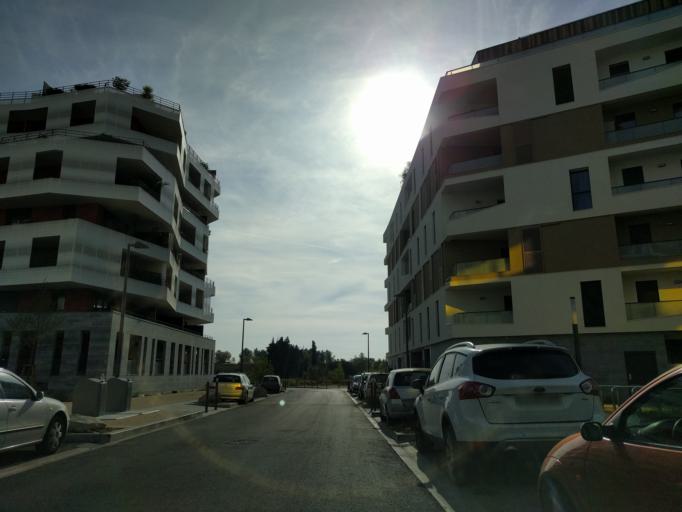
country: FR
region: Languedoc-Roussillon
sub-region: Departement de l'Herault
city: Montpellier
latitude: 43.5964
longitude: 3.9020
